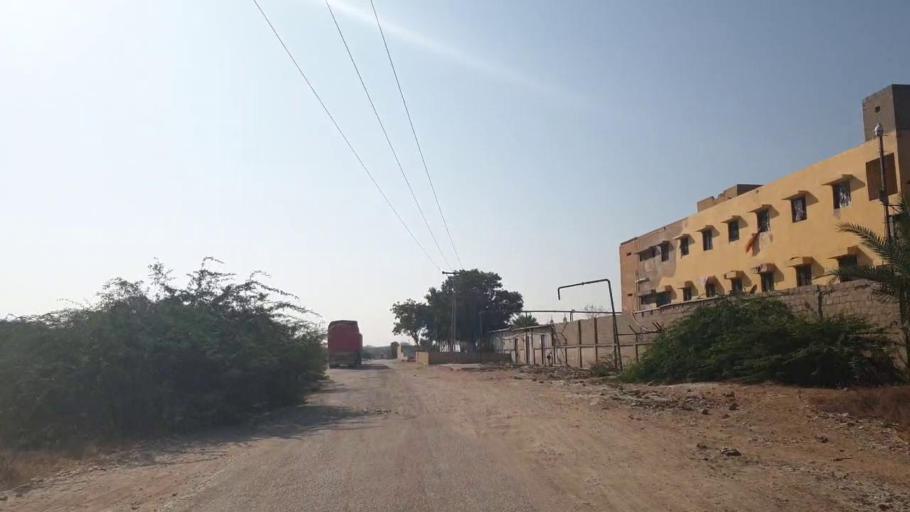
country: PK
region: Sindh
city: Thatta
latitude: 25.1559
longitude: 67.7737
